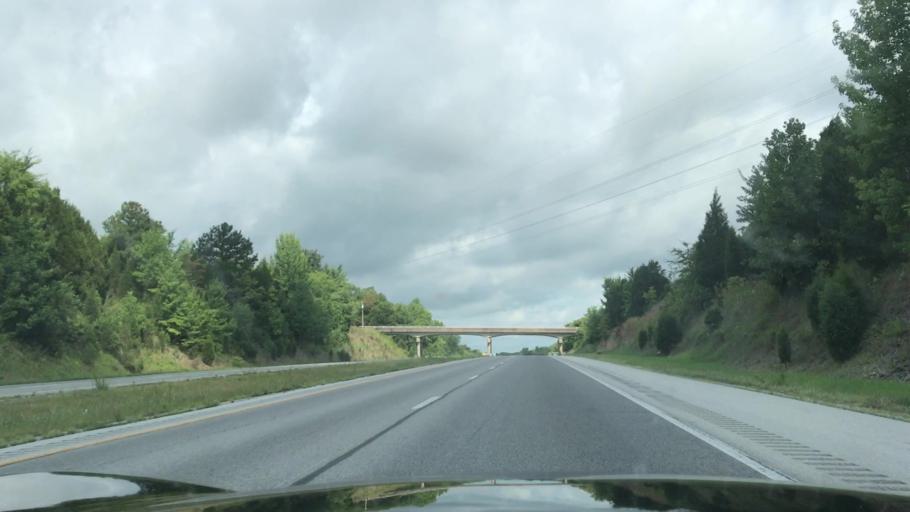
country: US
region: Kentucky
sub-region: Warren County
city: Bowling Green
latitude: 37.0257
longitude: -86.5327
